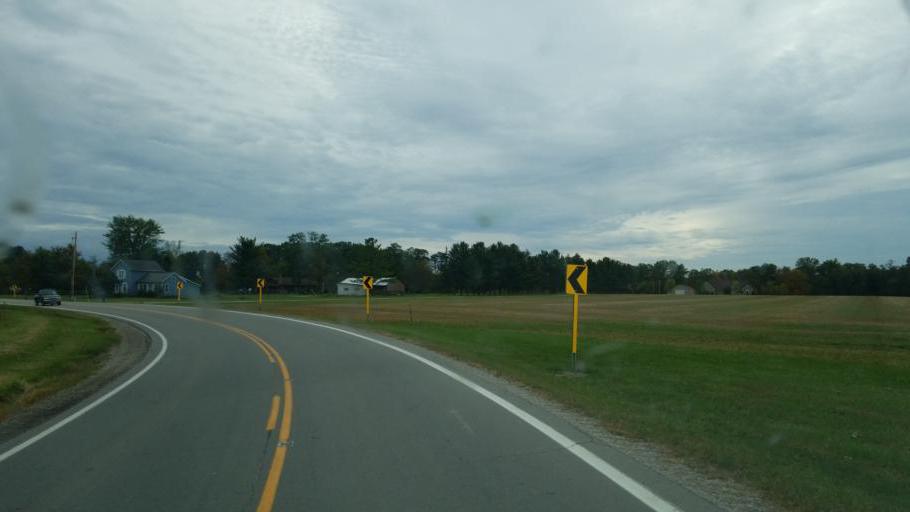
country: US
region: Ohio
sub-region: Huron County
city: Wakeman
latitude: 41.2745
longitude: -82.3940
